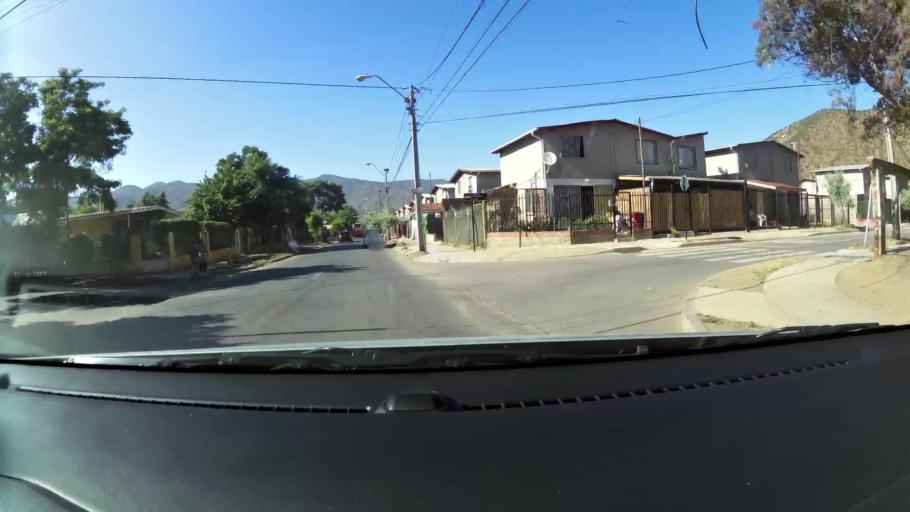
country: CL
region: Santiago Metropolitan
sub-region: Provincia de Chacabuco
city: Lampa
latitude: -33.3969
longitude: -71.1297
